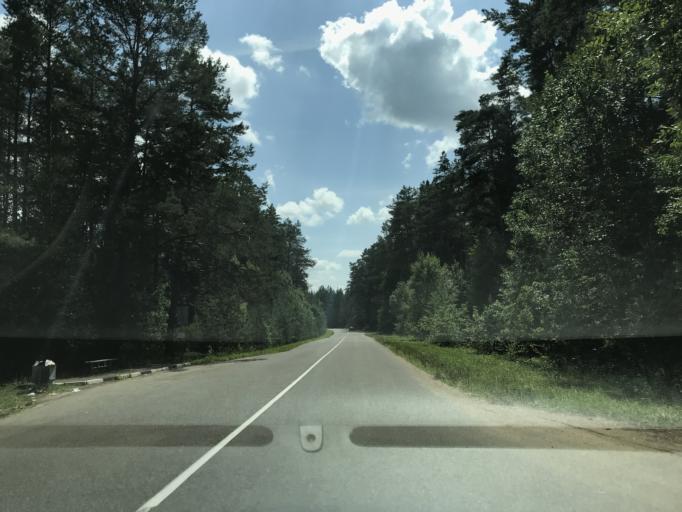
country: BY
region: Minsk
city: Rakaw
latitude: 53.9998
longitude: 26.9857
